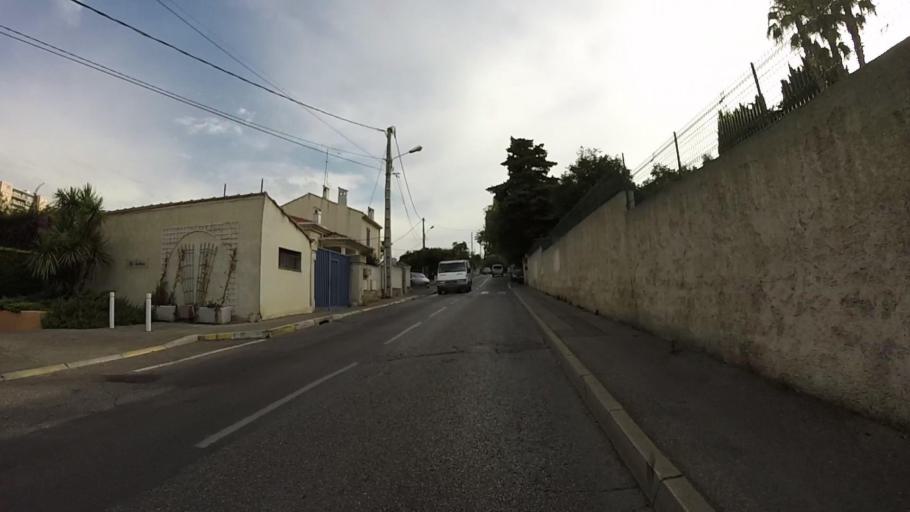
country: FR
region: Provence-Alpes-Cote d'Azur
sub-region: Departement des Alpes-Maritimes
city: Biot
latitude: 43.5927
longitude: 7.1060
